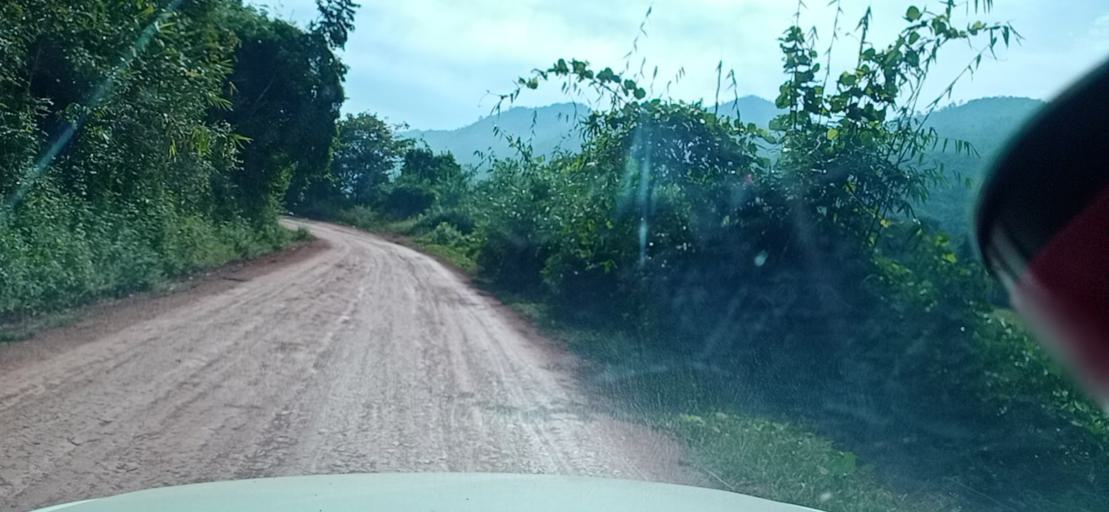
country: TH
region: Changwat Bueng Kan
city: Pak Khat
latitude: 18.6700
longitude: 103.1962
